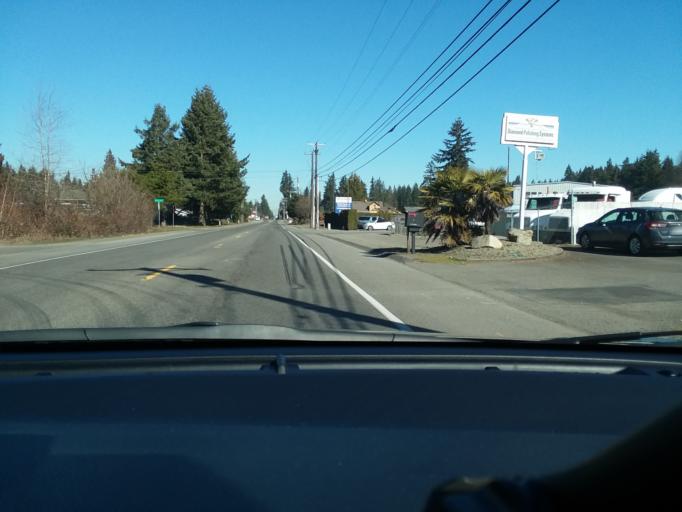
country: US
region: Washington
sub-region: Pierce County
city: Summit
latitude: 47.1771
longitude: -122.3571
